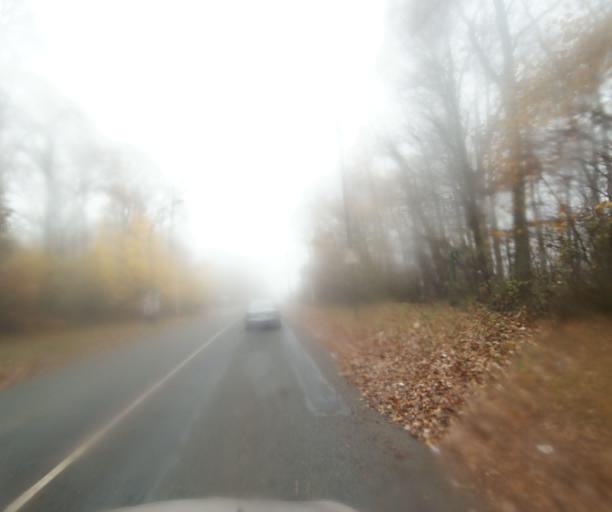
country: FR
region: Ile-de-France
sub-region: Departement de Seine-Saint-Denis
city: Vaujours
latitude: 48.9250
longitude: 2.5696
